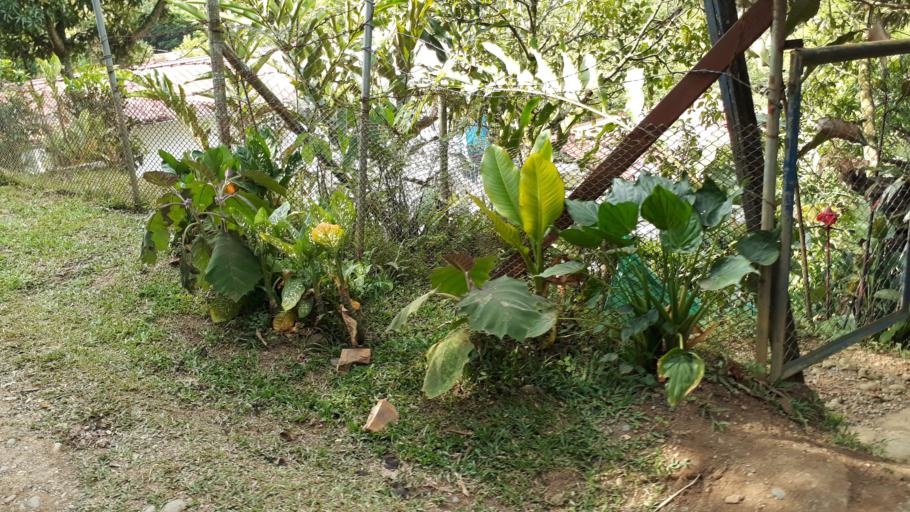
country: CO
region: Valle del Cauca
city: Jamundi
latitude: 3.2210
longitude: -76.6258
